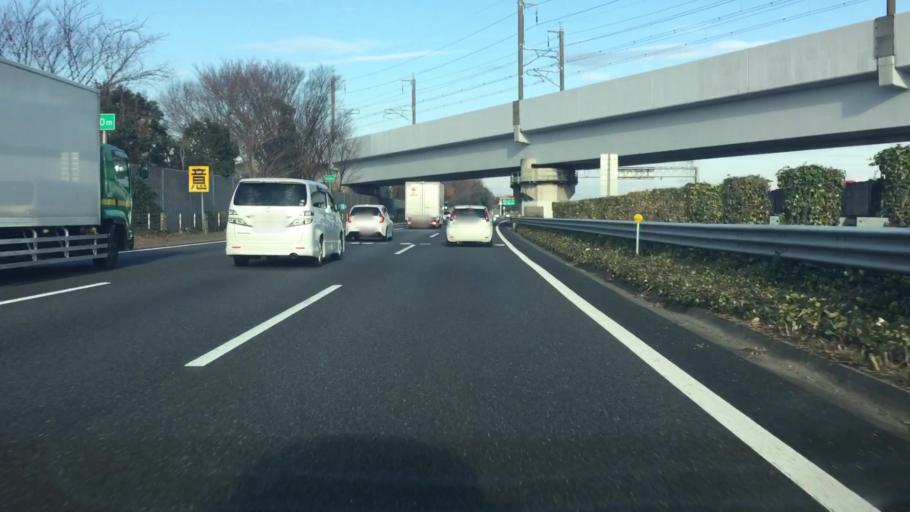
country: JP
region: Saitama
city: Honjo
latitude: 36.2331
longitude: 139.1495
